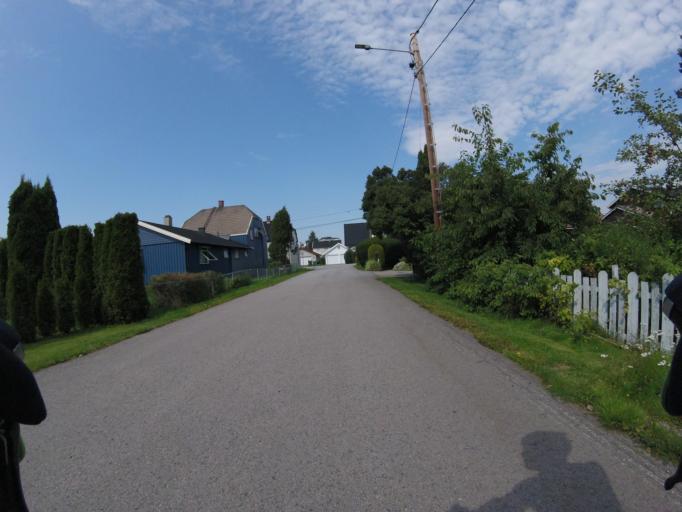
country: NO
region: Akershus
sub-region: Skedsmo
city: Lillestrom
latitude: 59.9568
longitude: 11.0629
